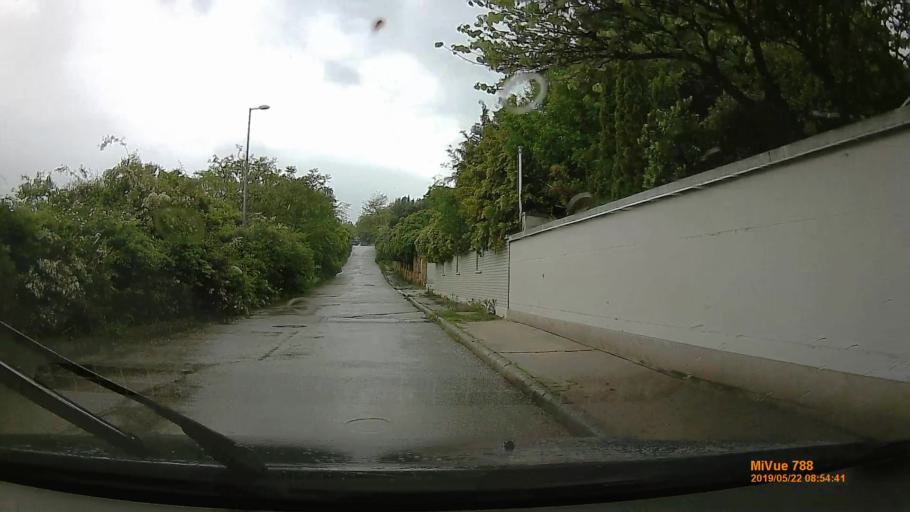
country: HU
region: Budapest
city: Budapest II. keruelet
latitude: 47.5336
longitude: 19.0062
